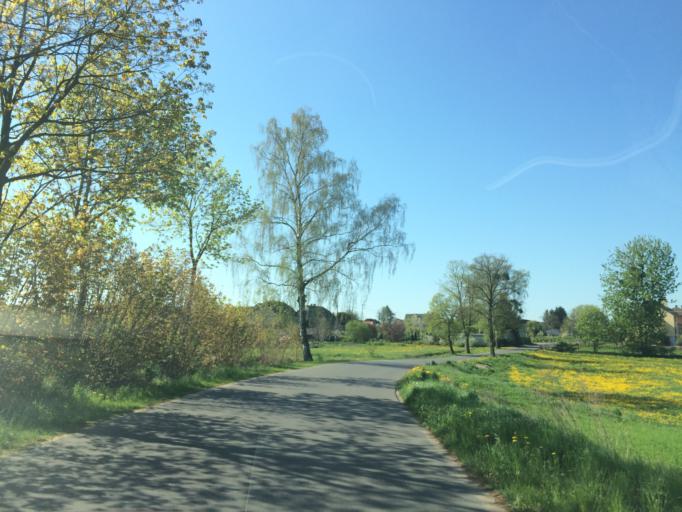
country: PL
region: Warmian-Masurian Voivodeship
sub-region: Powiat nowomiejski
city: Nowe Miasto Lubawskie
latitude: 53.4829
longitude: 19.5741
